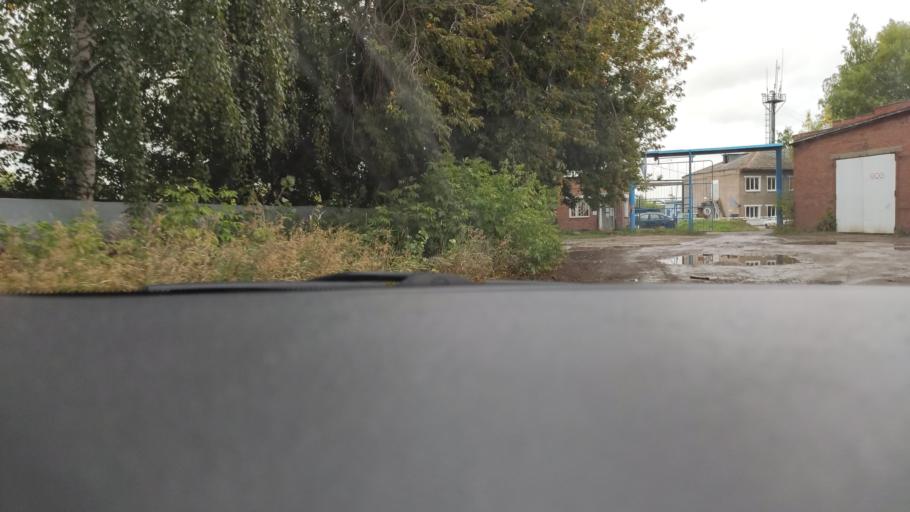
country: RU
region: Perm
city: Krasnokamsk
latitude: 58.0782
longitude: 55.7652
